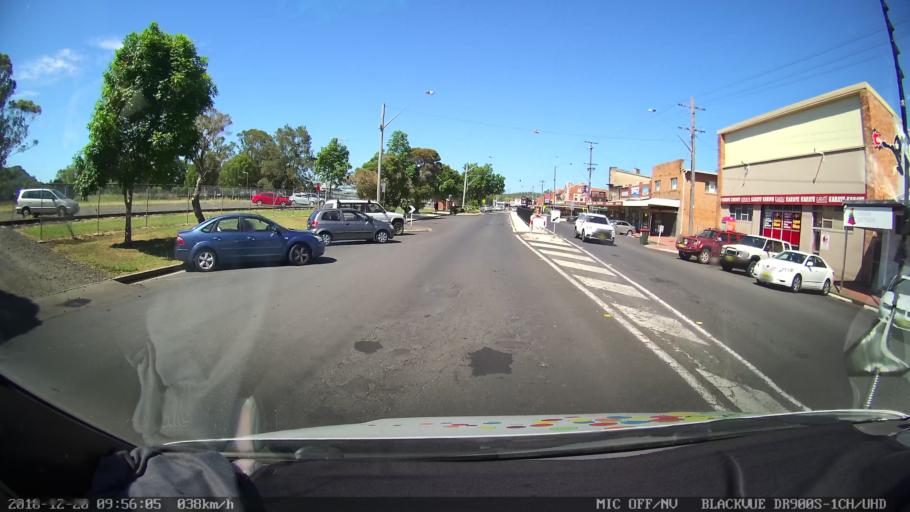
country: AU
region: New South Wales
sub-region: Lismore Municipality
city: Lismore
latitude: -28.8088
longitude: 153.2705
